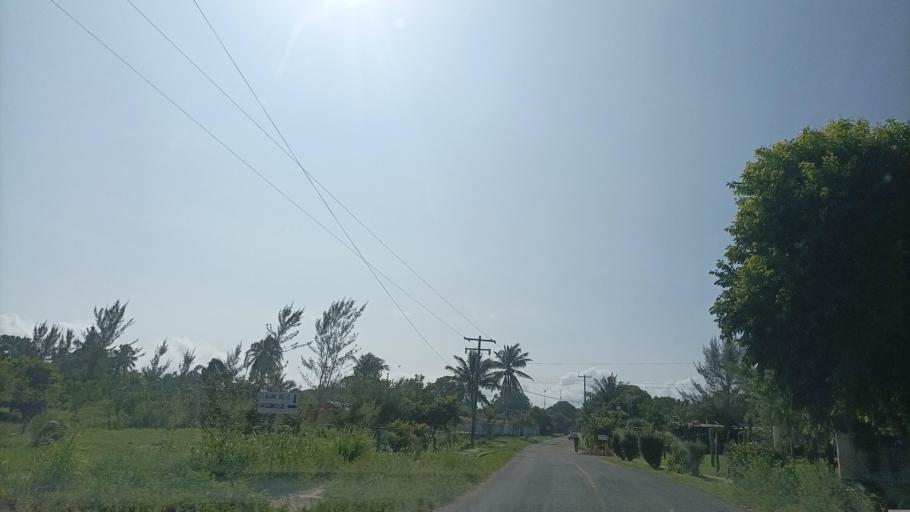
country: MX
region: Veracruz
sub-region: Pajapan
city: Pajapan
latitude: 18.2172
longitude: -94.6146
